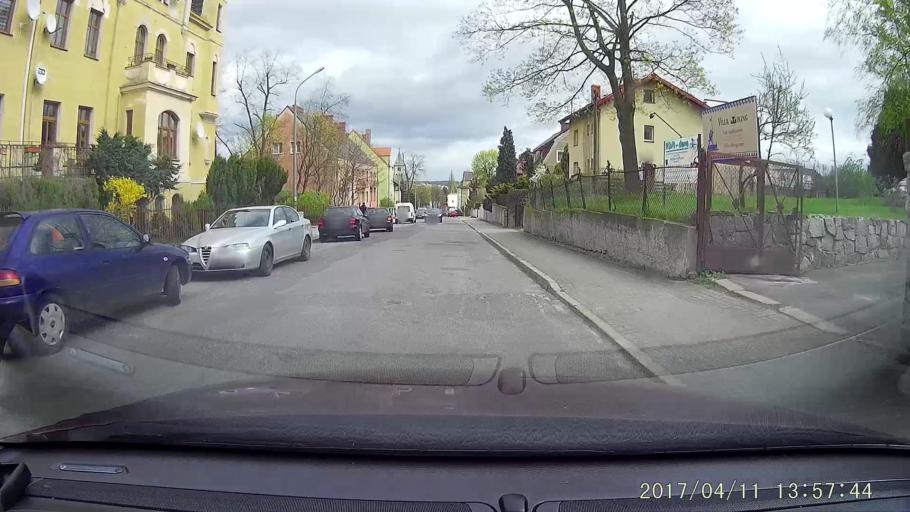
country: PL
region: Lower Silesian Voivodeship
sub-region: Powiat zgorzelecki
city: Zgorzelec
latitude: 51.1383
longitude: 15.0086
